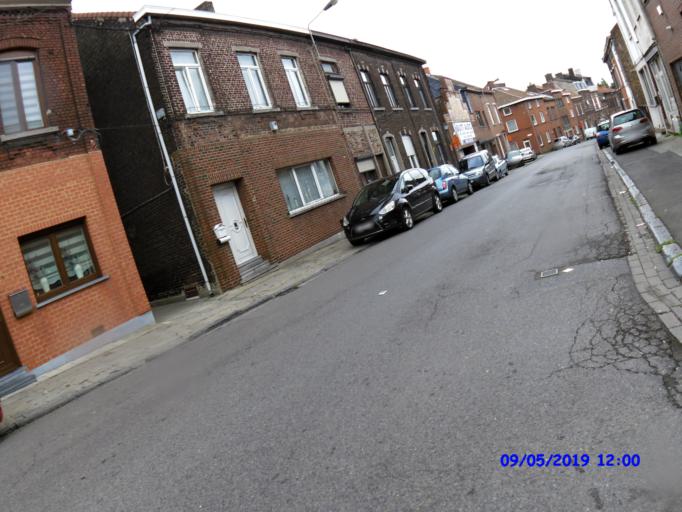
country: BE
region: Wallonia
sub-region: Province du Hainaut
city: Charleroi
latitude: 50.3992
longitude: 4.4817
